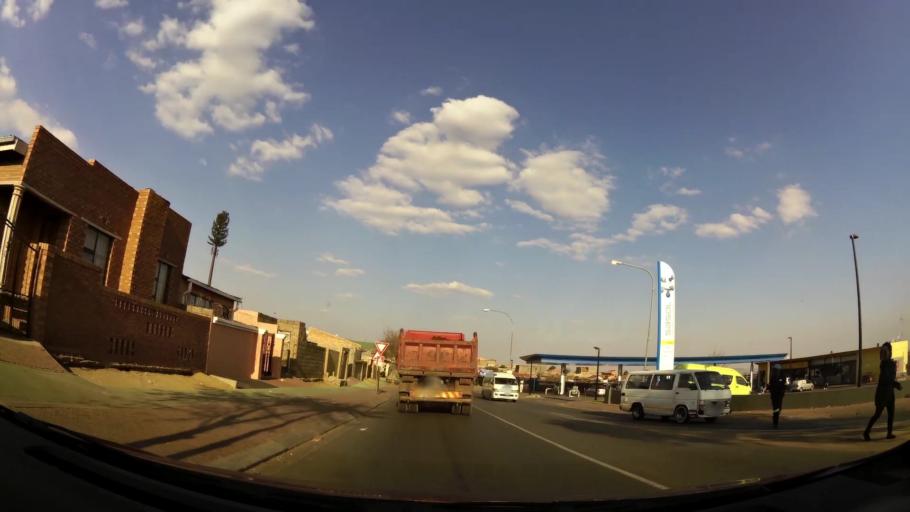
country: ZA
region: Gauteng
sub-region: City of Johannesburg Metropolitan Municipality
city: Soweto
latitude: -26.2215
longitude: 27.8894
